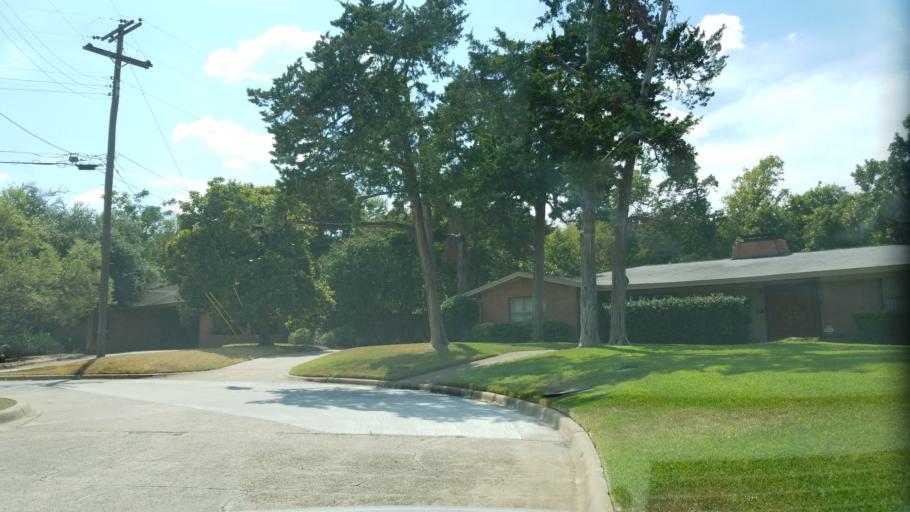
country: US
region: Texas
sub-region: Dallas County
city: Dallas
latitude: 32.7637
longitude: -96.8396
